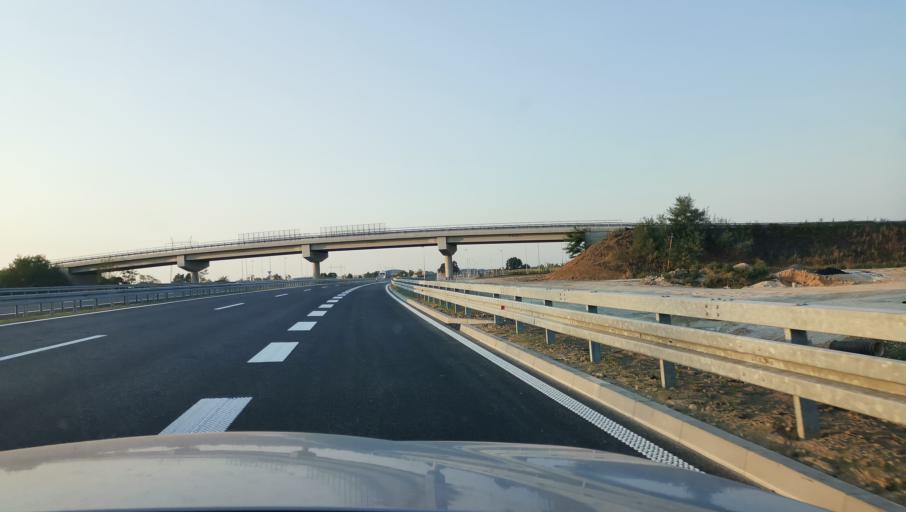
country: RS
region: Central Serbia
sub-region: Kolubarski Okrug
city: Ub
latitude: 44.4033
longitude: 20.0945
